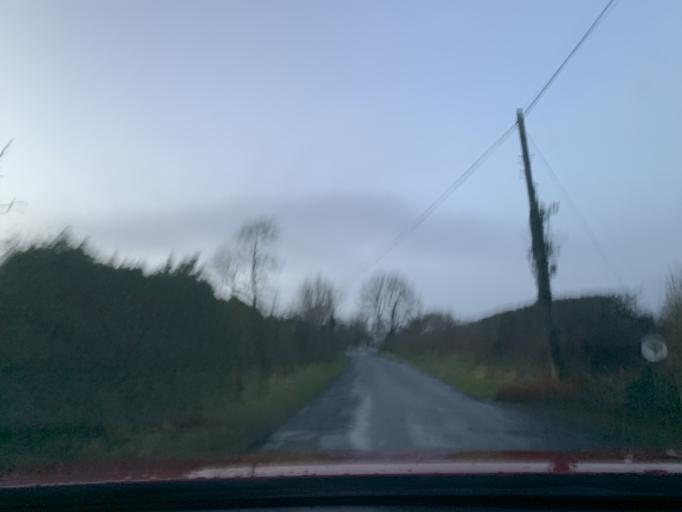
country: IE
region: Connaught
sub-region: Sligo
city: Ballymote
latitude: 54.1209
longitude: -8.5789
